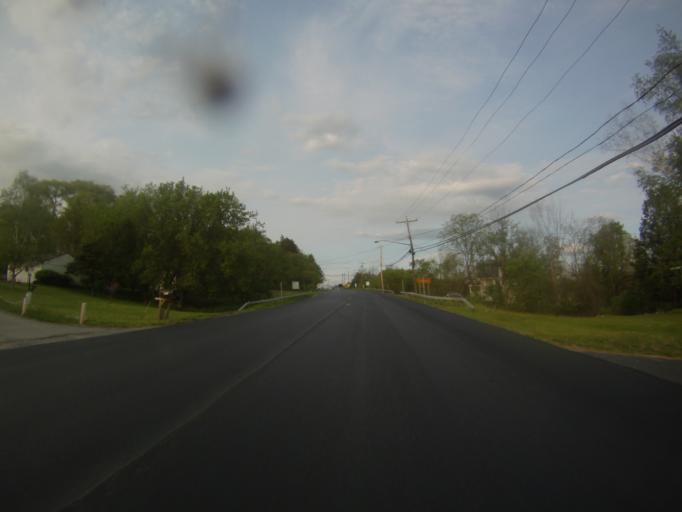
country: US
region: New York
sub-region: Essex County
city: Ticonderoga
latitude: 43.8467
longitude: -73.4392
